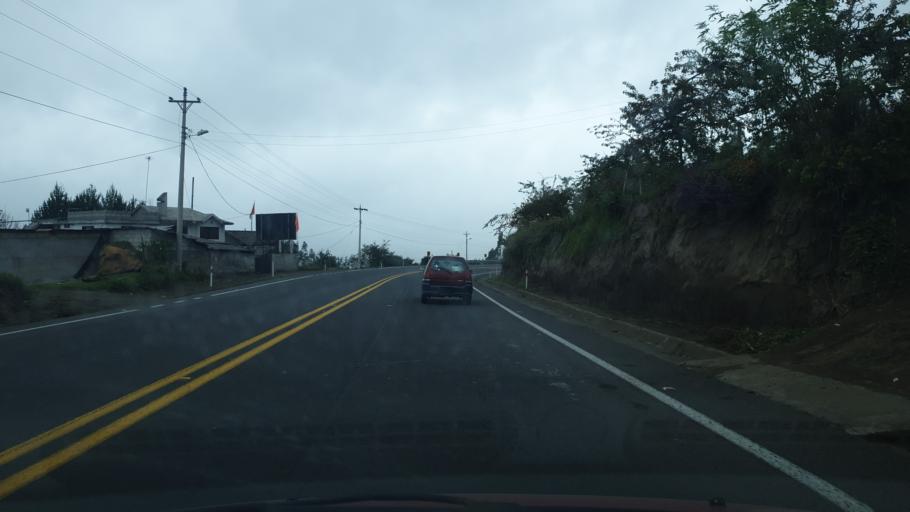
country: EC
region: Tungurahua
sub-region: Canton Quero
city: Quero
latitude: -1.3822
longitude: -78.6470
